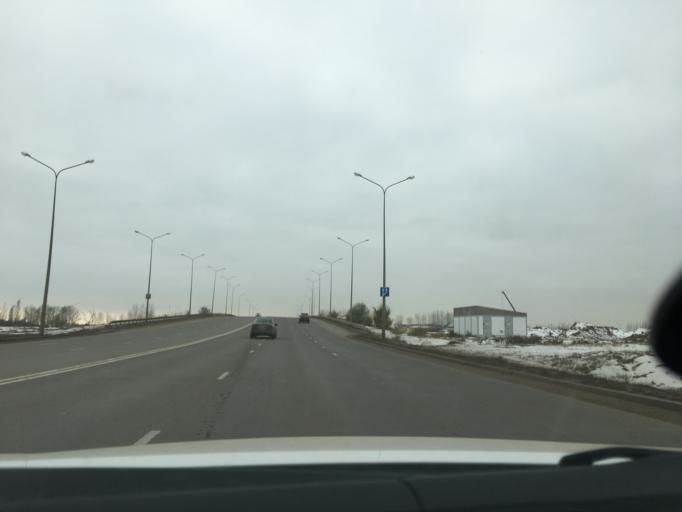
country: KZ
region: Astana Qalasy
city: Astana
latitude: 51.1424
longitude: 71.5264
